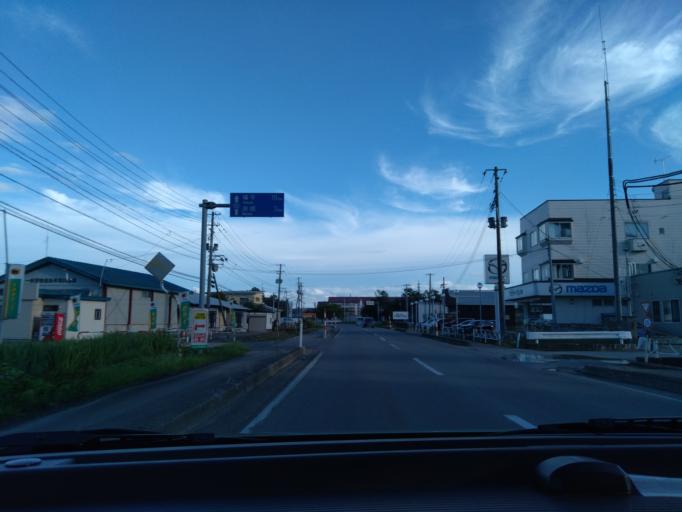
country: JP
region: Akita
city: Omagari
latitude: 39.4304
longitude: 140.4863
